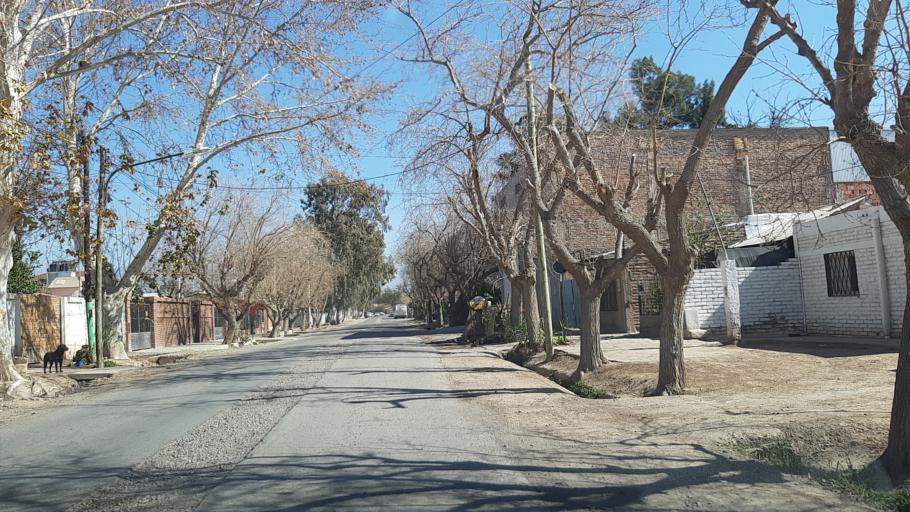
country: AR
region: San Juan
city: San Juan
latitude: -31.5362
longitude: -68.5894
